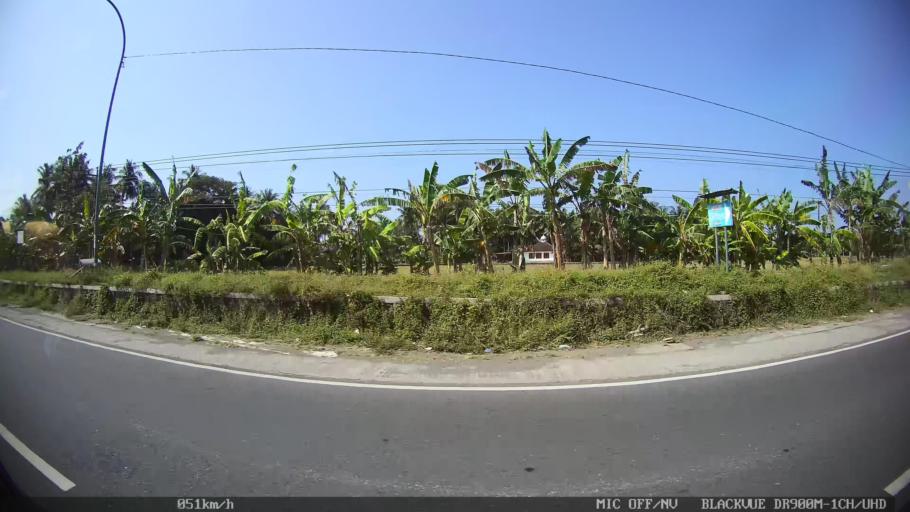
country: ID
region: Daerah Istimewa Yogyakarta
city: Srandakan
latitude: -7.9302
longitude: 110.1953
